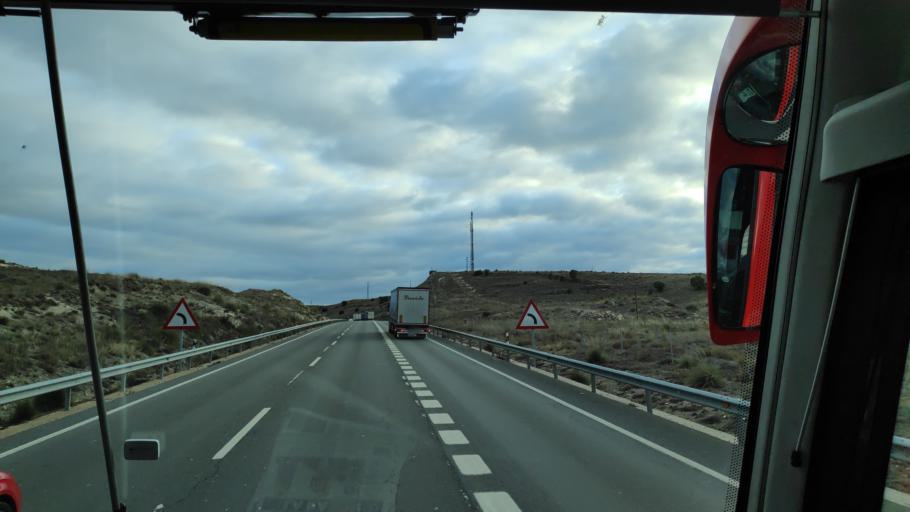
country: ES
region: Madrid
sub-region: Provincia de Madrid
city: Tielmes
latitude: 40.2039
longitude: -3.3149
